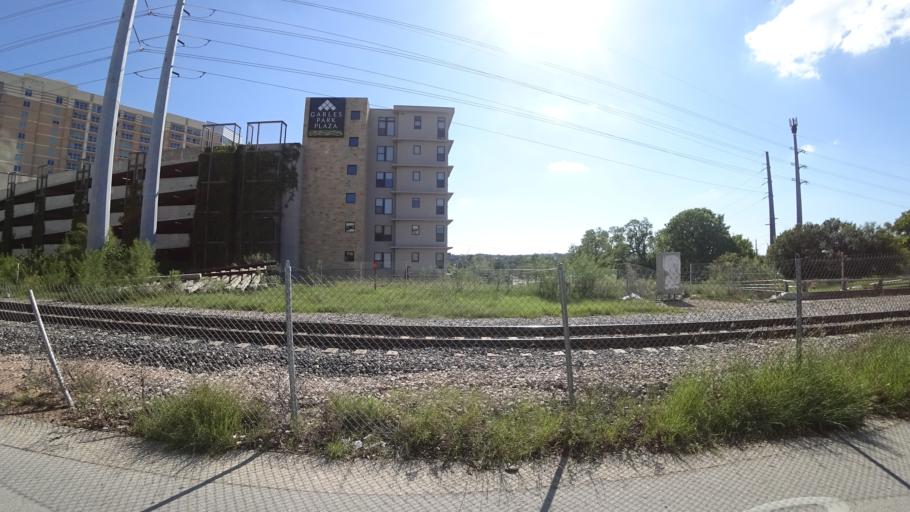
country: US
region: Texas
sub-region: Travis County
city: Austin
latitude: 30.2690
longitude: -97.7549
